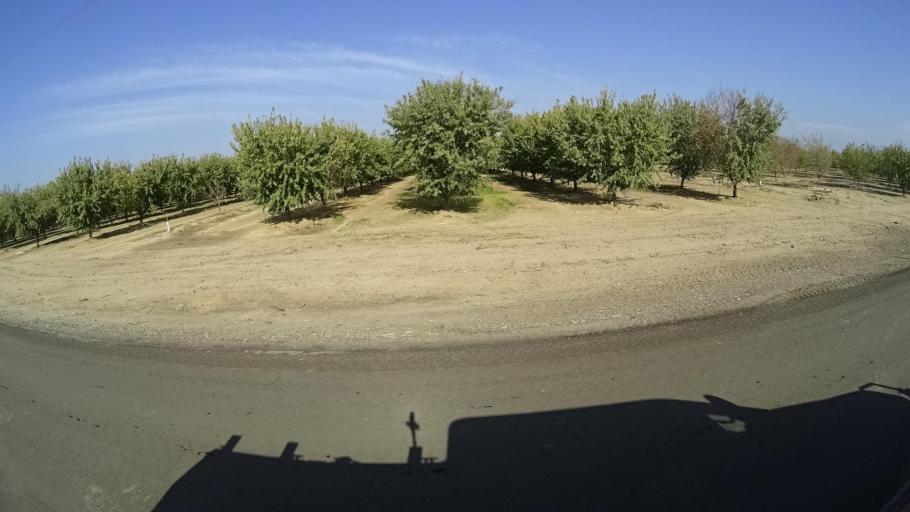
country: US
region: California
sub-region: Kern County
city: McFarland
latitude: 35.6600
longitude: -119.1755
